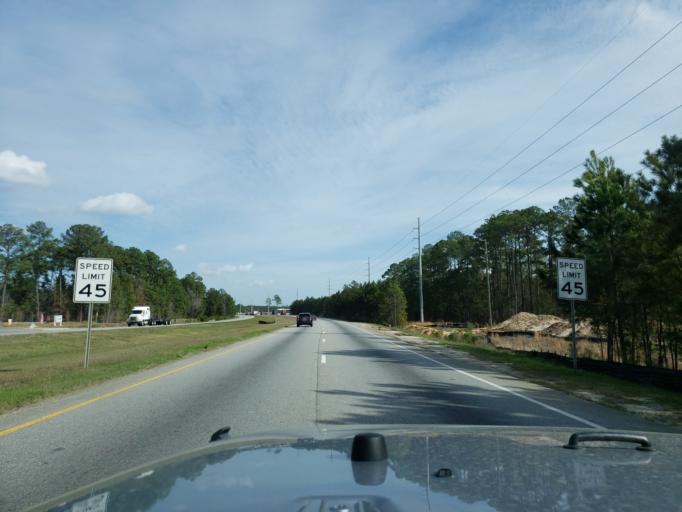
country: US
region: Georgia
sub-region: Chatham County
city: Pooler
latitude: 32.1639
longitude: -81.2318
